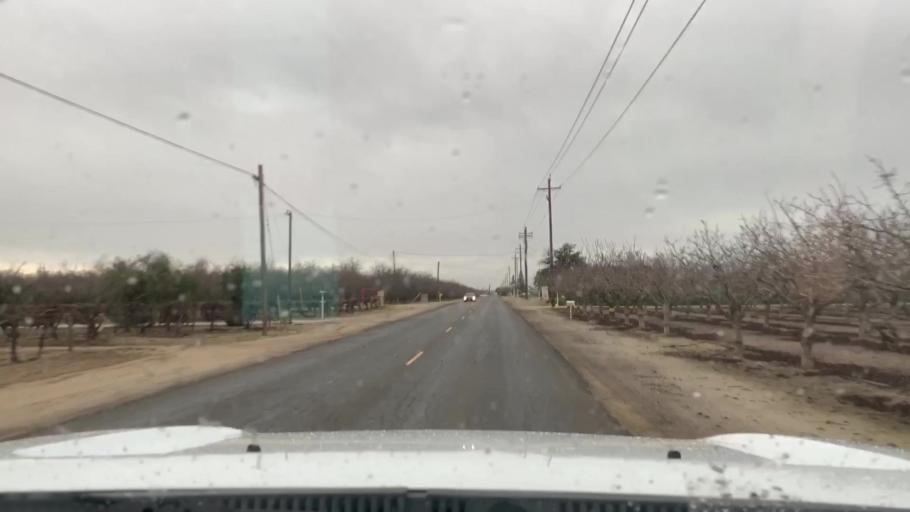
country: US
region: California
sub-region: Kern County
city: Shafter
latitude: 35.5115
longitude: -119.2960
